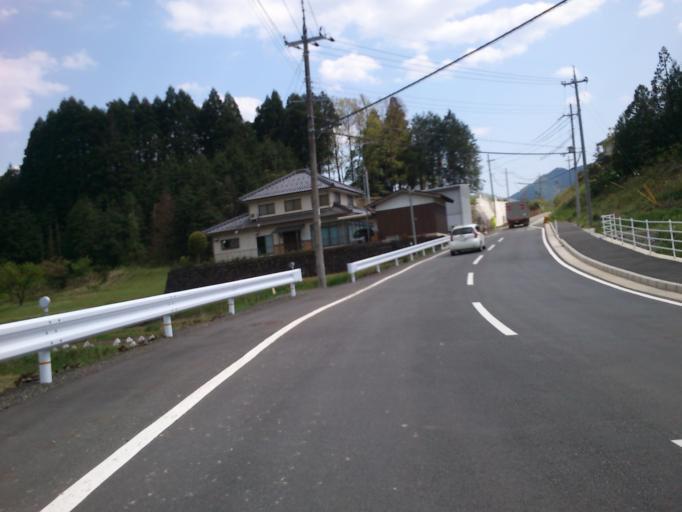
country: JP
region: Kyoto
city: Fukuchiyama
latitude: 35.3415
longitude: 134.9337
